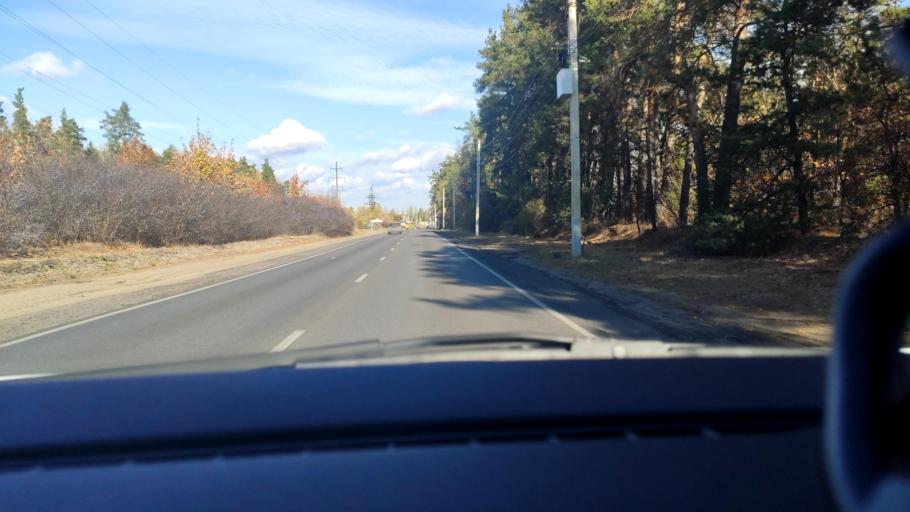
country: RU
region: Voronezj
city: Pridonskoy
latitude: 51.6300
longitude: 39.0820
